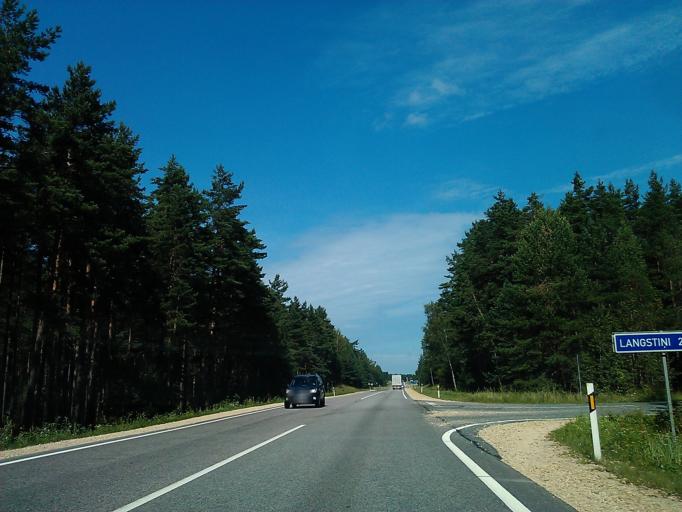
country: LV
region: Riga
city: Bergi
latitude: 57.0019
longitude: 24.3074
